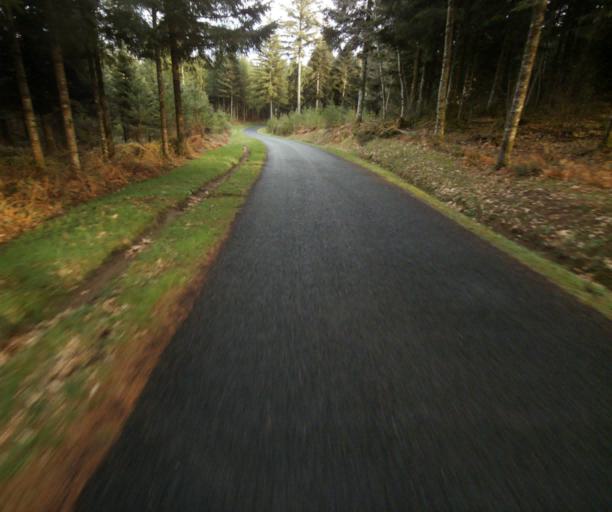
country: FR
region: Limousin
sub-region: Departement de la Correze
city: Argentat
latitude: 45.2131
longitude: 1.9437
